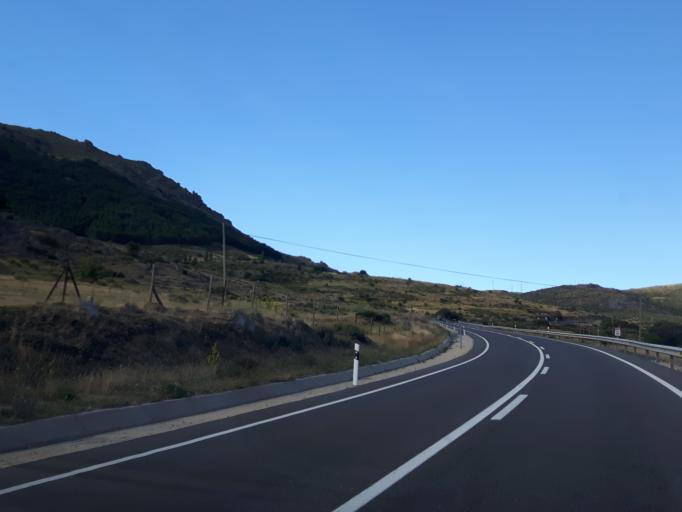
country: ES
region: Castille and Leon
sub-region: Provincia de Avila
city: Mengamunoz
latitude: 40.4944
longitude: -5.0049
